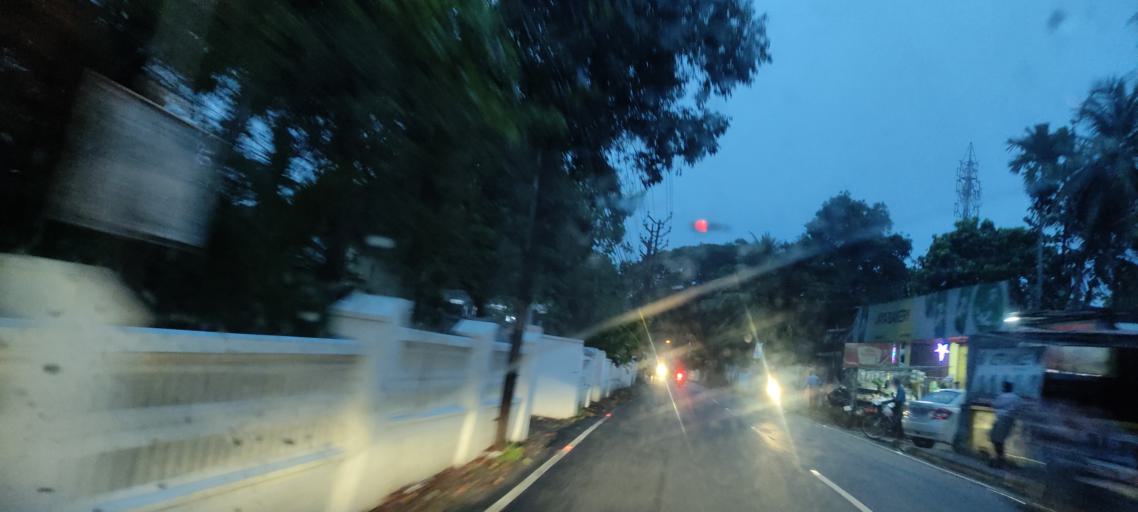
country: IN
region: Kerala
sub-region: Ernakulam
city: Cochin
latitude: 9.9126
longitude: 76.2924
